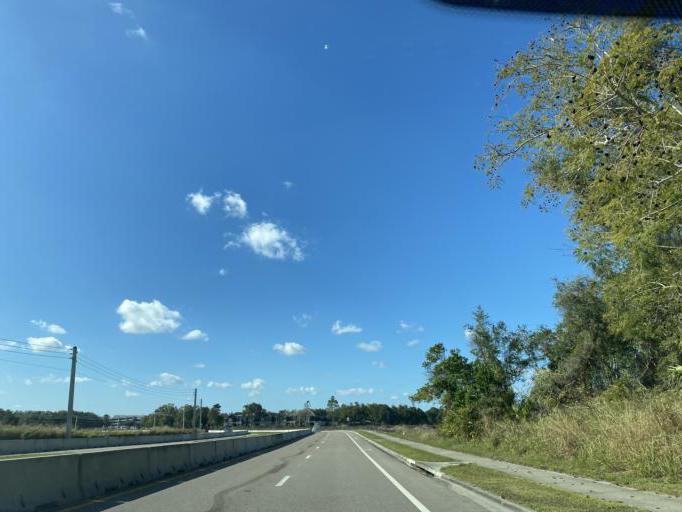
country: US
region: Florida
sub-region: Seminole County
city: Heathrow
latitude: 28.7990
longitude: -81.3507
